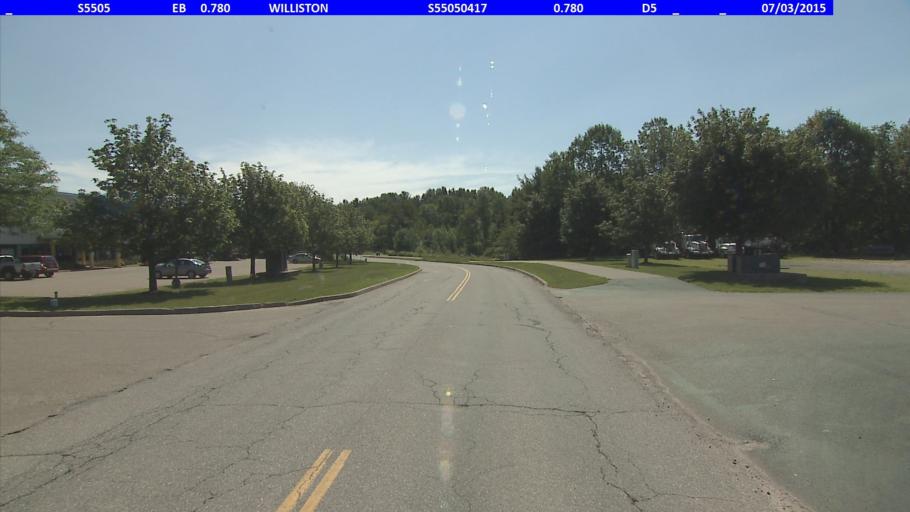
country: US
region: Vermont
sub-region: Chittenden County
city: Essex Junction
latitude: 44.4452
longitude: -73.1275
